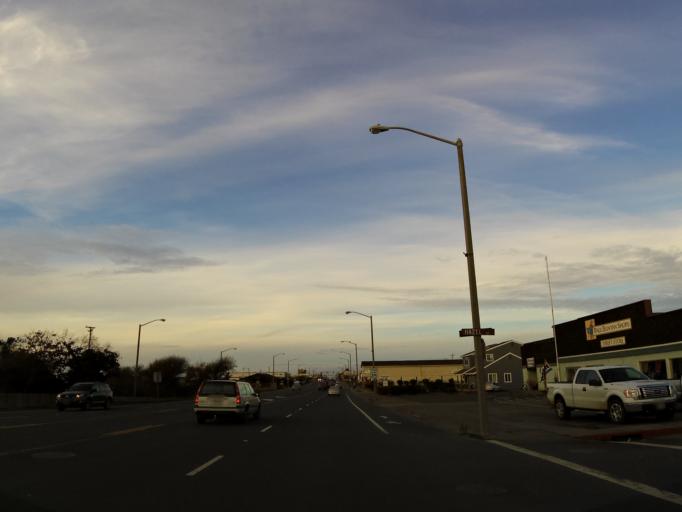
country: US
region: California
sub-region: Mendocino County
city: Fort Bragg
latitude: 39.4380
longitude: -123.8060
